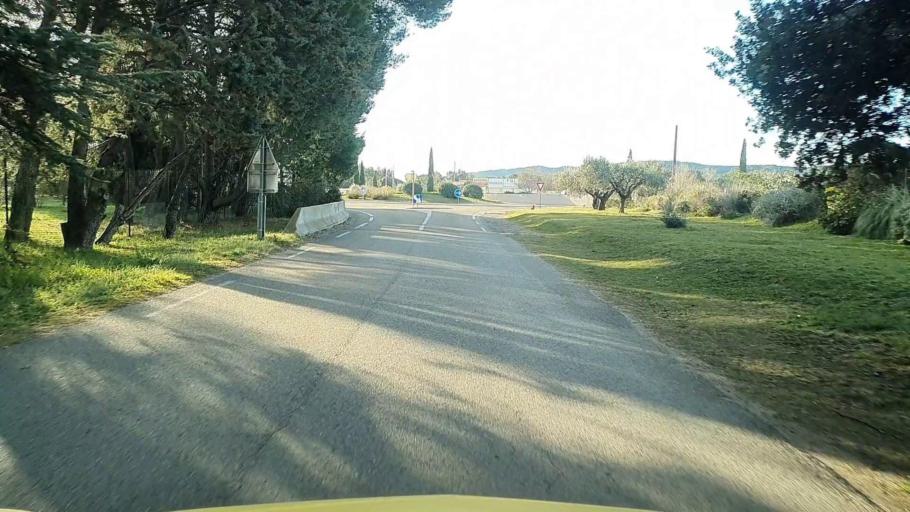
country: FR
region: Languedoc-Roussillon
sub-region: Departement du Gard
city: Castillon-du-Gard
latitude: 43.9556
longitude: 4.5514
